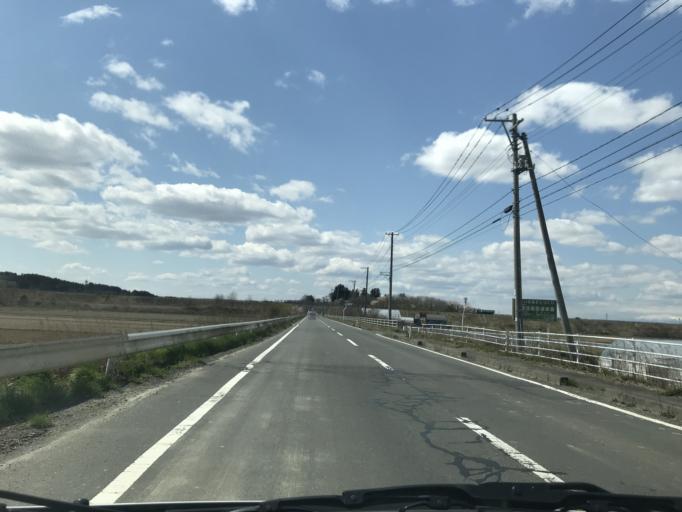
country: JP
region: Miyagi
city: Wakuya
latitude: 38.6485
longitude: 141.2669
